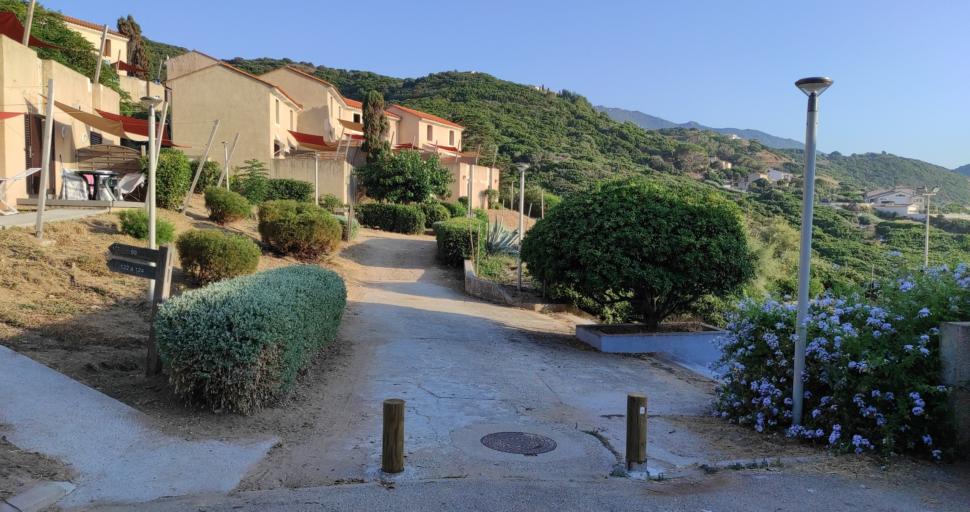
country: FR
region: Corsica
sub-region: Departement de la Corse-du-Sud
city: Alata
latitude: 41.9832
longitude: 8.6706
